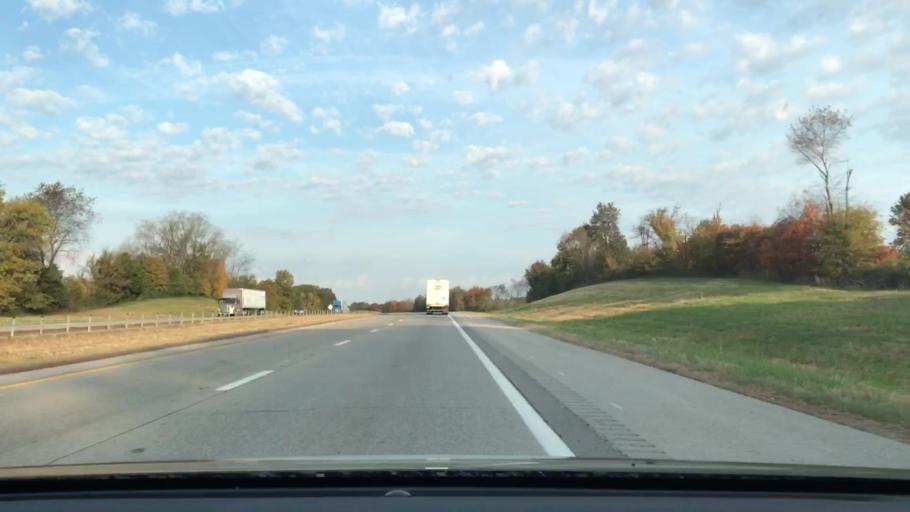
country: US
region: Kentucky
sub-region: Trigg County
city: Cadiz
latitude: 36.8371
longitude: -87.6680
